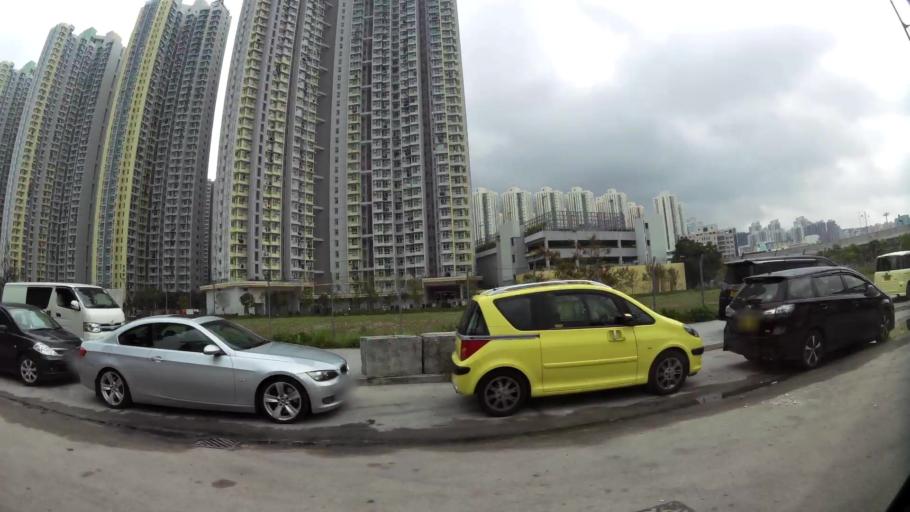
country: HK
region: Kowloon City
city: Kowloon
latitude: 22.3280
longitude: 114.2031
